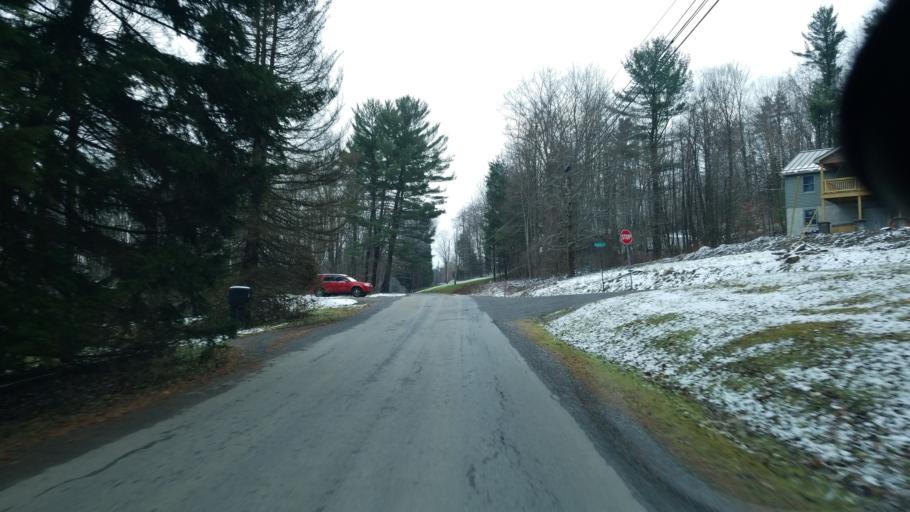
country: US
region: Pennsylvania
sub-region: Clearfield County
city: Treasure Lake
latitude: 41.0942
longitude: -78.6377
